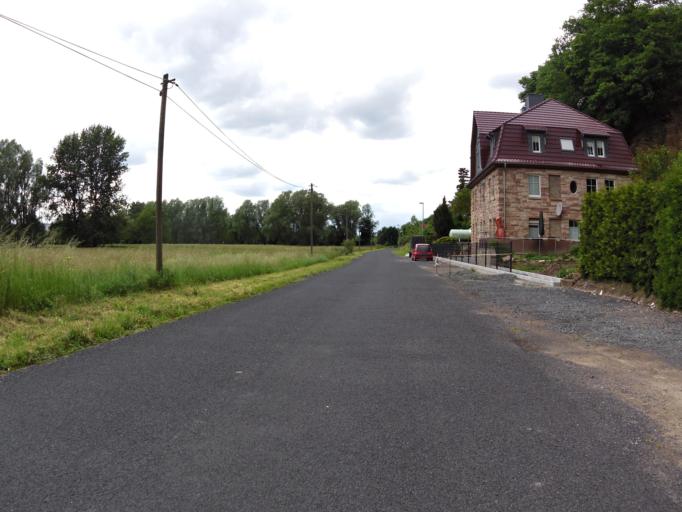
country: DE
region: Thuringia
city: Bad Salzungen
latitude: 50.8197
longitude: 10.2393
